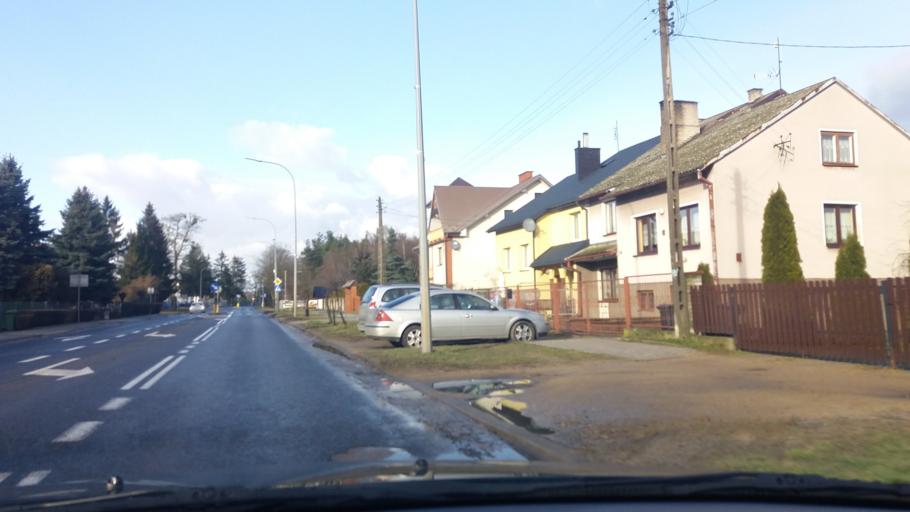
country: PL
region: Masovian Voivodeship
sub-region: Powiat przasnyski
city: Chorzele
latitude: 53.2650
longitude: 20.8974
